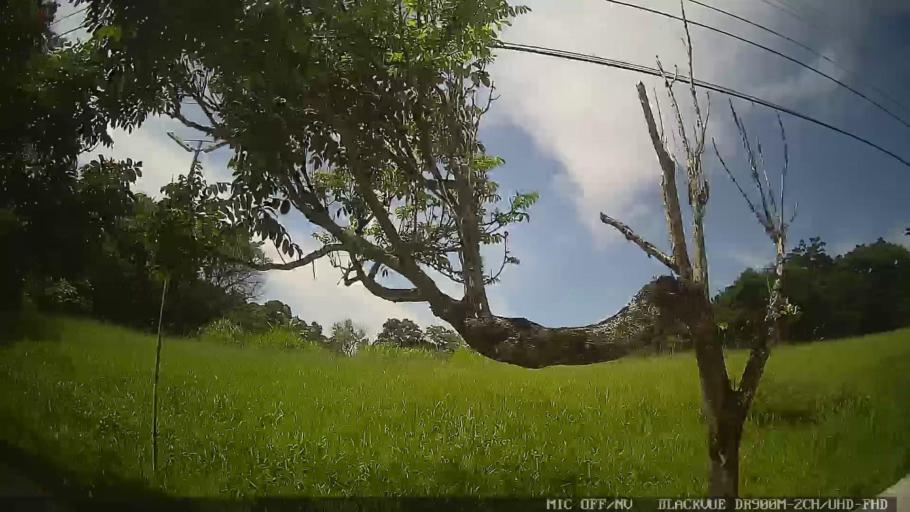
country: BR
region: Sao Paulo
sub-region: Mogi das Cruzes
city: Mogi das Cruzes
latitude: -23.4658
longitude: -46.2584
